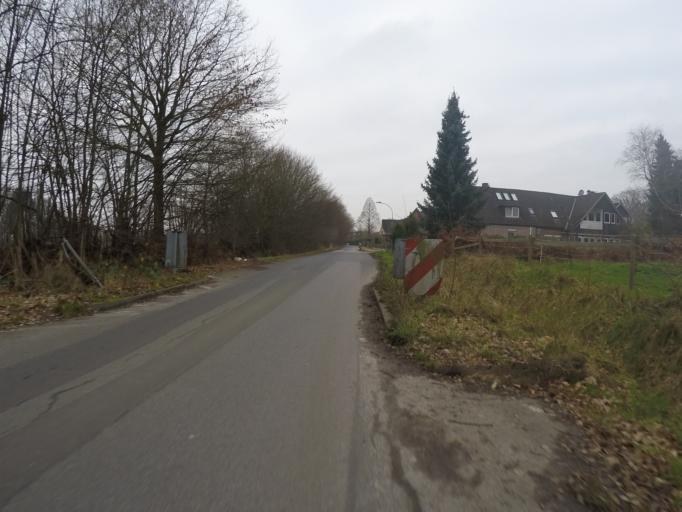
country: DE
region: Schleswig-Holstein
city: Borstel-Hohenraden
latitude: 53.6963
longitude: 9.8303
